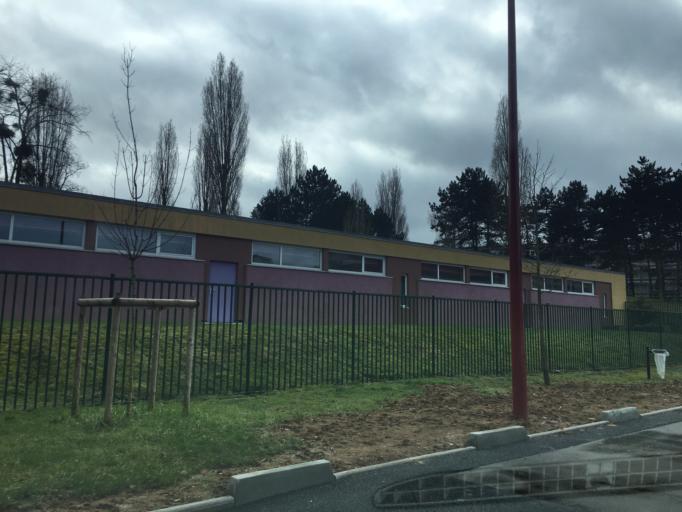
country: FR
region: Ile-de-France
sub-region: Departement du Val-d'Oise
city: Arnouville
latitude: 49.0021
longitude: 2.4260
